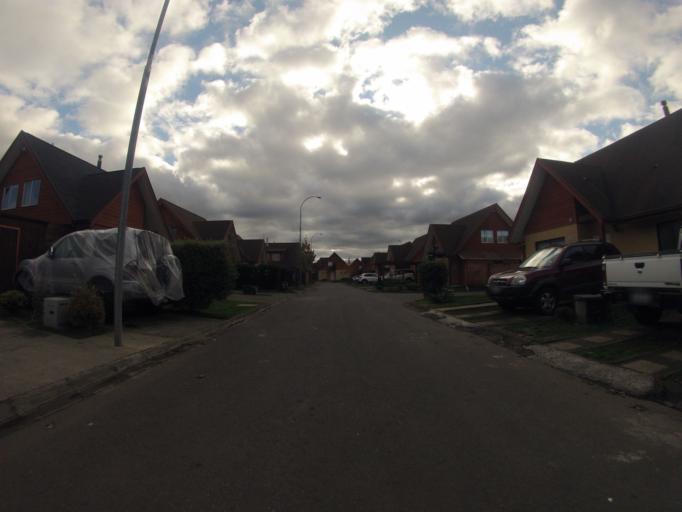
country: CL
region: Araucania
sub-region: Provincia de Cautin
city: Temuco
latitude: -38.7392
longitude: -72.6457
